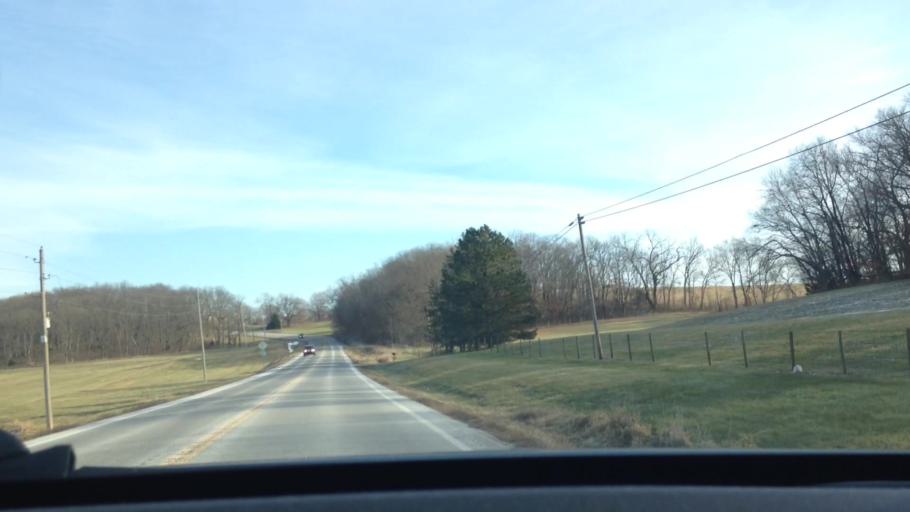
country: US
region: Missouri
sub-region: Platte County
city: Platte City
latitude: 39.3843
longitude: -94.8218
